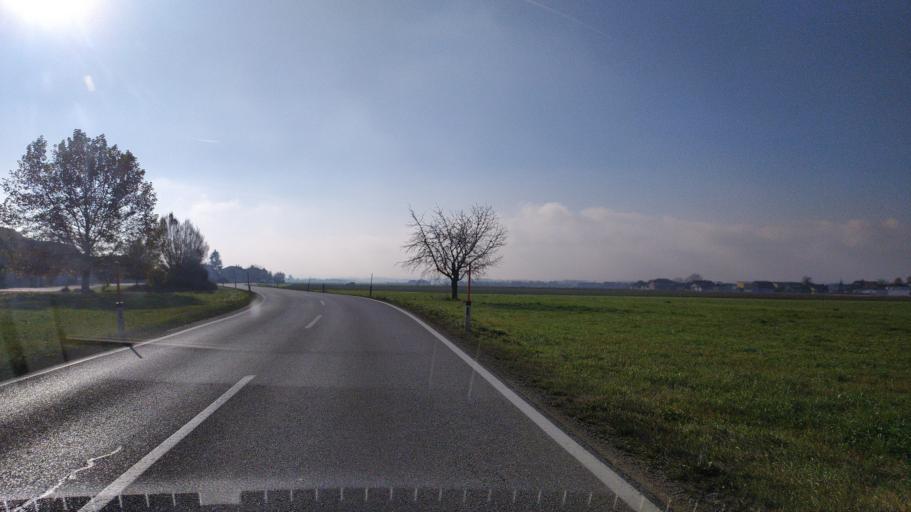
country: AT
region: Upper Austria
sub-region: Politischer Bezirk Perg
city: Perg
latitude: 48.2319
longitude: 14.6229
